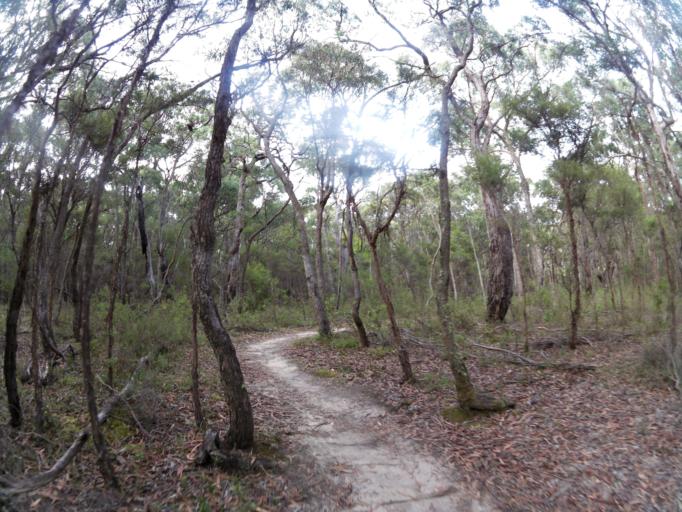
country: AU
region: Victoria
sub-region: Colac-Otway
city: Colac
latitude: -38.4912
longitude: 143.6989
